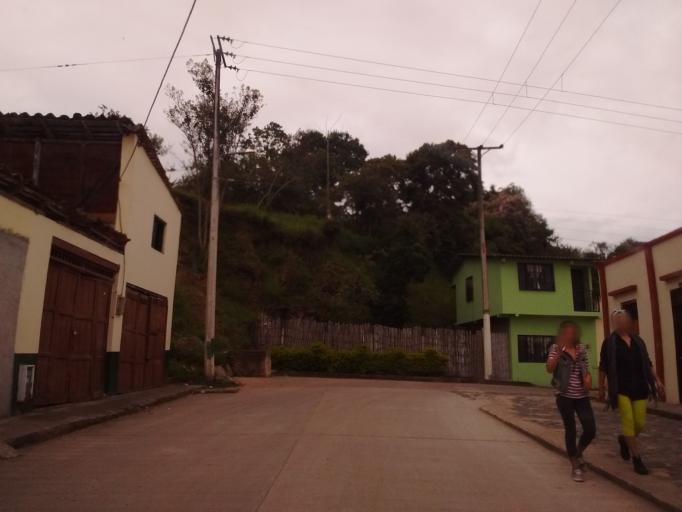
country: CO
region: Huila
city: San Agustin
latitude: 1.8829
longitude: -76.2707
